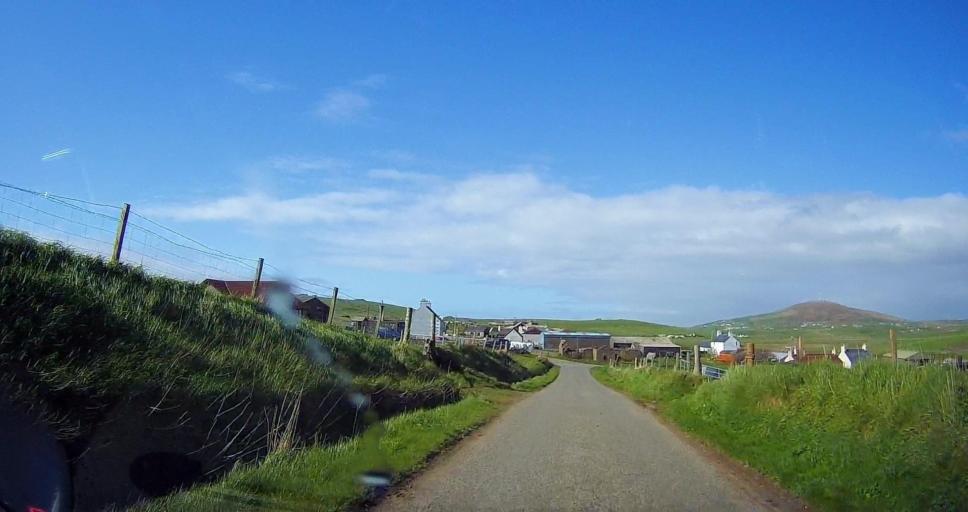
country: GB
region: Scotland
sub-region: Shetland Islands
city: Sandwick
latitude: 59.9090
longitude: -1.3345
